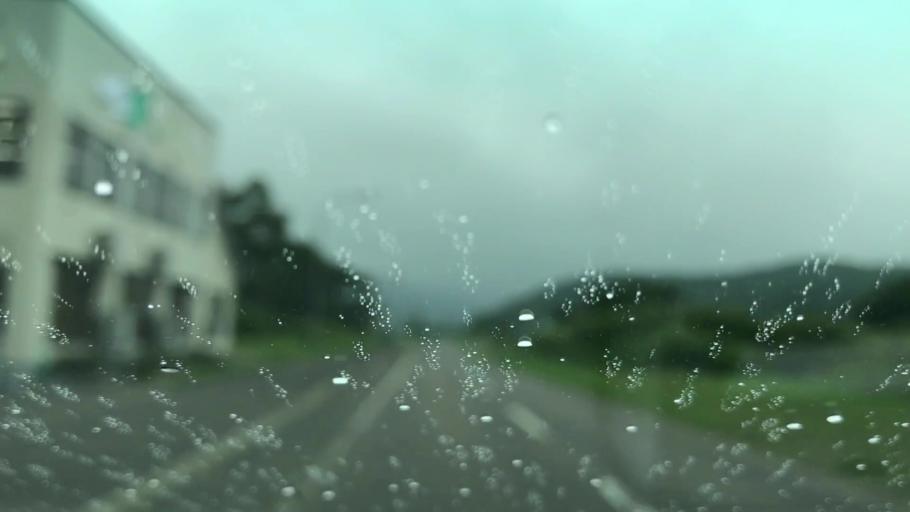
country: JP
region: Hokkaido
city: Iwanai
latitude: 42.7494
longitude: 140.2832
